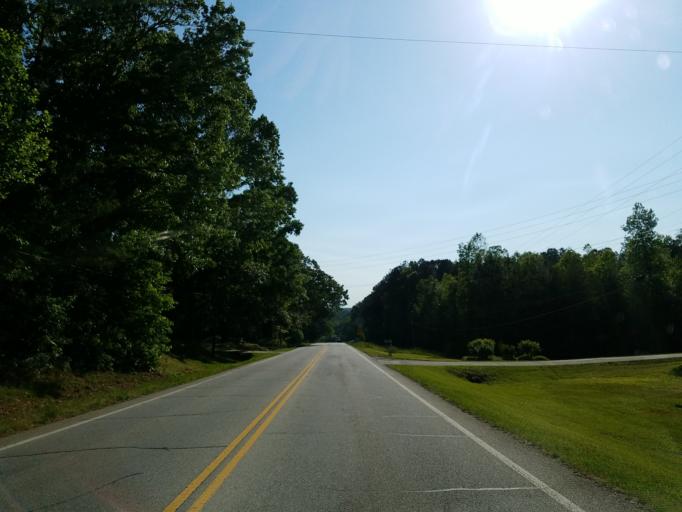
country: US
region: Georgia
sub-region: Paulding County
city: Dallas
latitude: 33.9100
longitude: -84.8661
